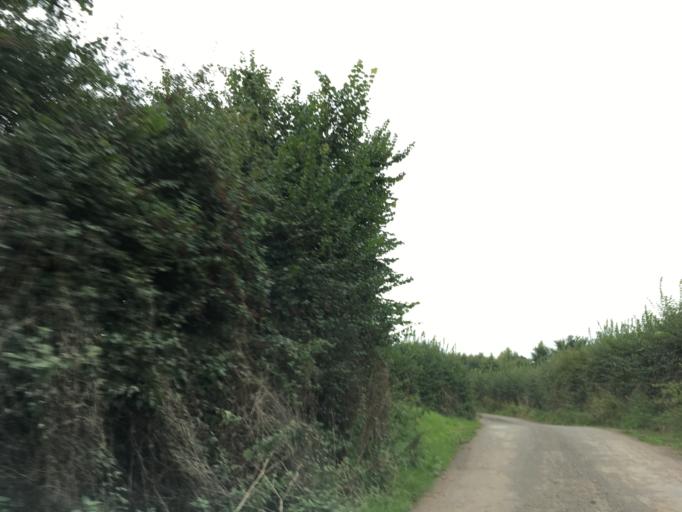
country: GB
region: England
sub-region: South Gloucestershire
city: Falfield
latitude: 51.6465
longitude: -2.4674
